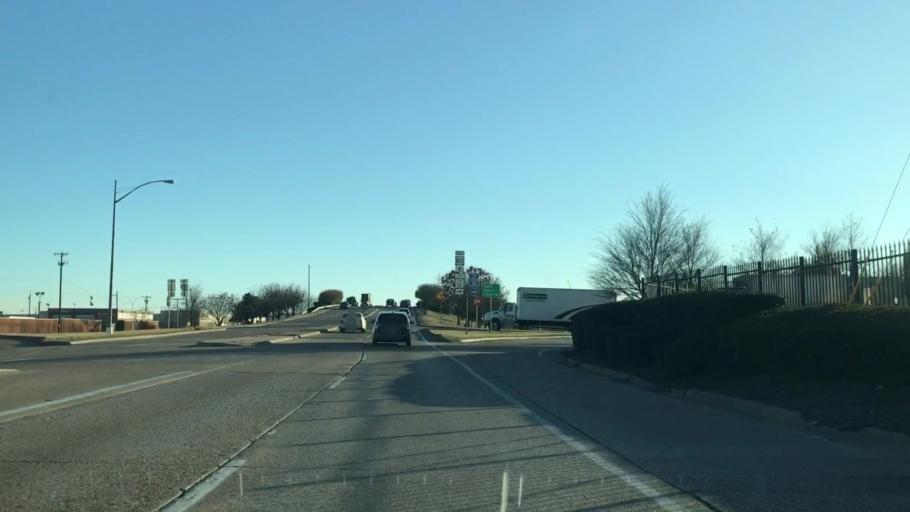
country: US
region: Texas
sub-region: Dallas County
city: Mesquite
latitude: 32.7996
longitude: -96.6683
